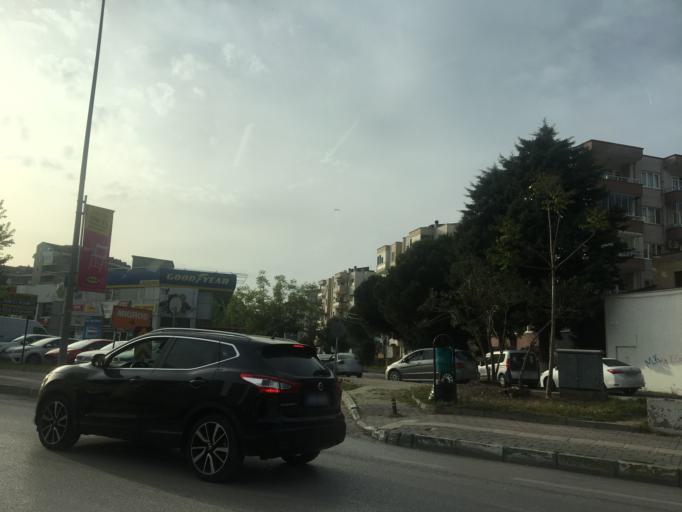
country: TR
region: Bursa
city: Yildirim
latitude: 40.2120
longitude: 28.9894
